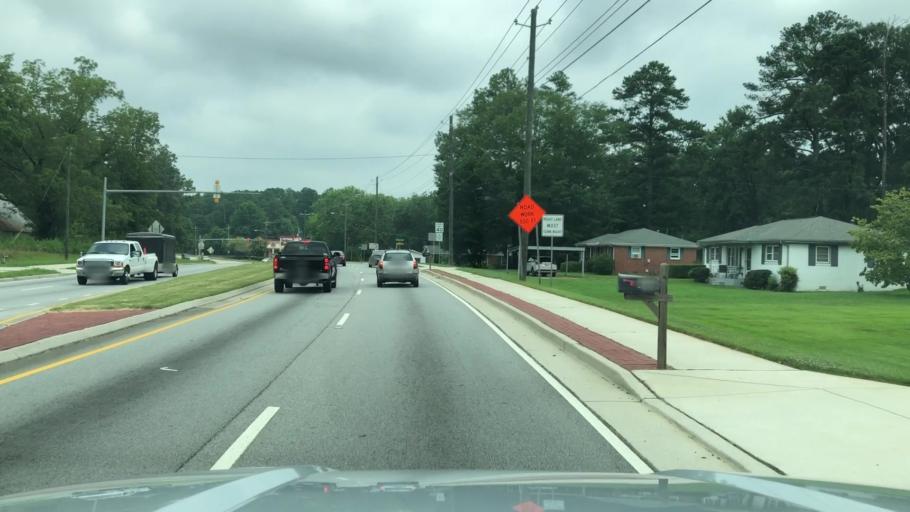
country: US
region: Georgia
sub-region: Cobb County
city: Mableton
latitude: 33.8387
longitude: -84.5768
